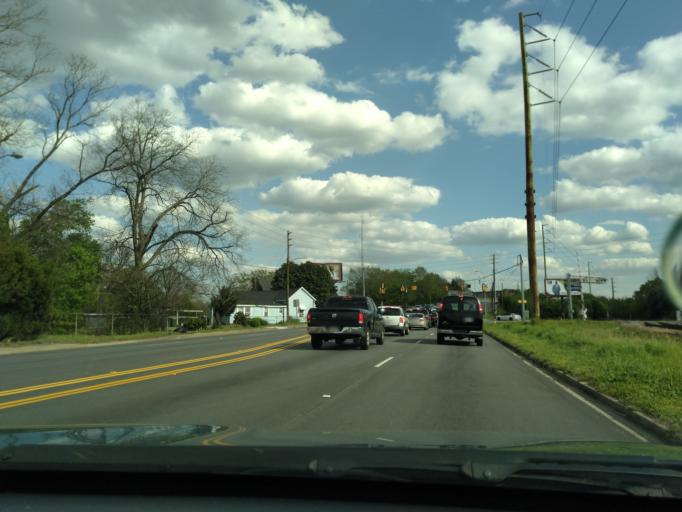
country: US
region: South Carolina
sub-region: Florence County
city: Florence
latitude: 34.2016
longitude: -79.7646
